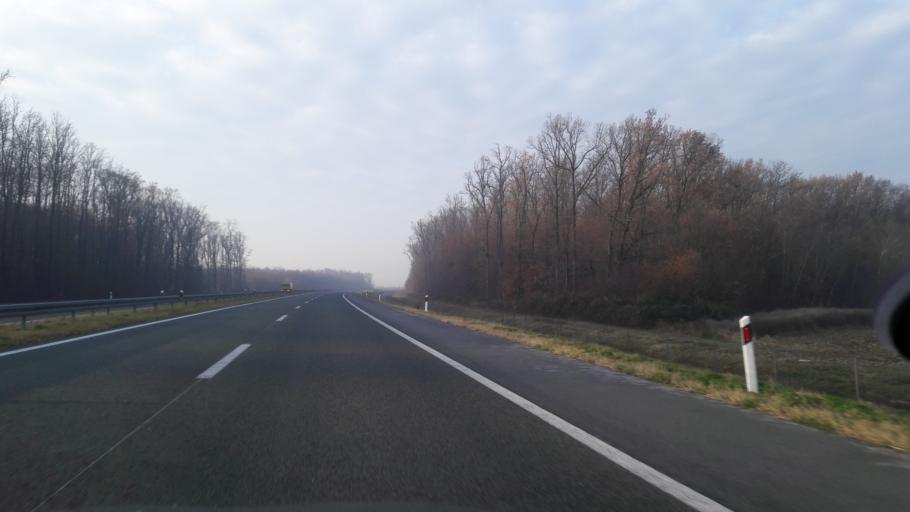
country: HR
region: Osjecko-Baranjska
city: Vuka
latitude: 45.4196
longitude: 18.4501
